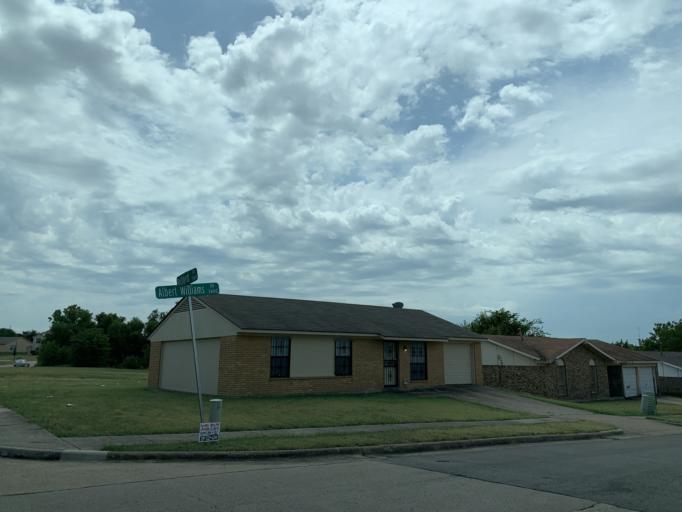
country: US
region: Texas
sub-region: Dallas County
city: DeSoto
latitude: 32.6580
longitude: -96.8124
